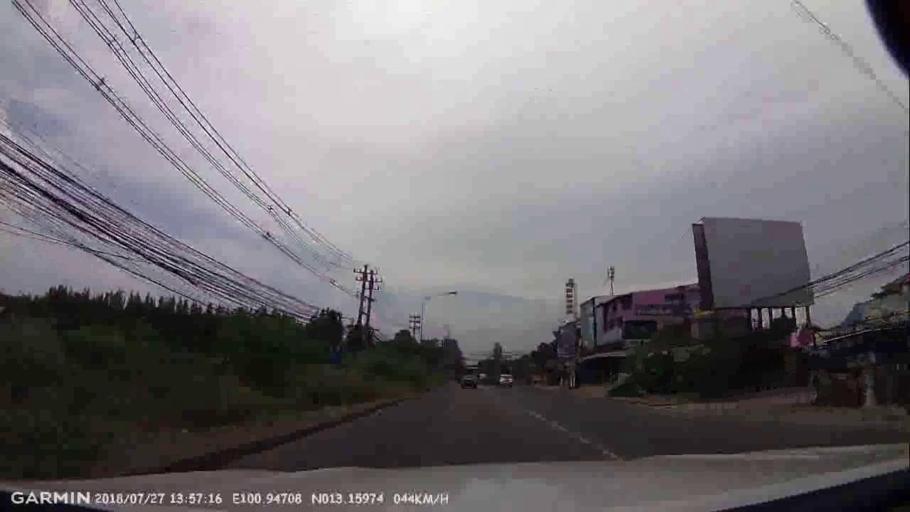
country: TH
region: Chon Buri
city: Si Racha
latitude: 13.1598
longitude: 100.9470
